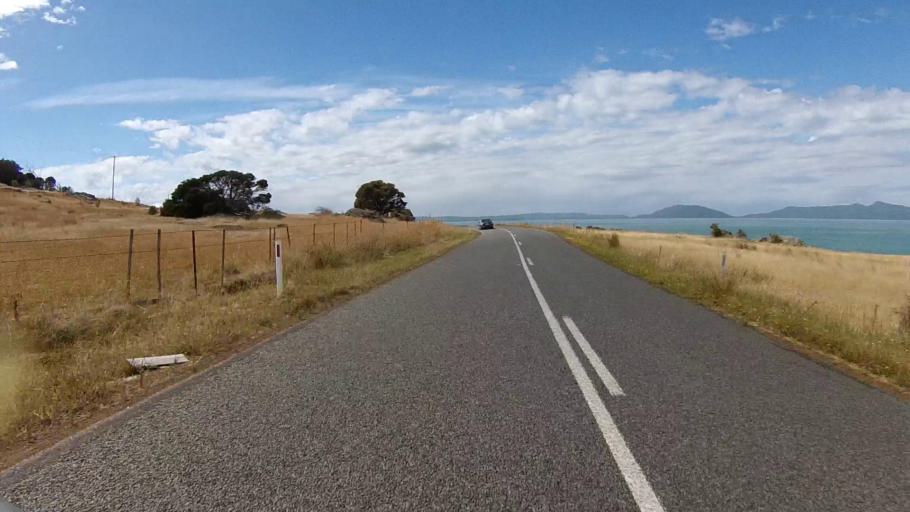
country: AU
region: Tasmania
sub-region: Sorell
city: Sorell
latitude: -42.1734
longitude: 148.0714
